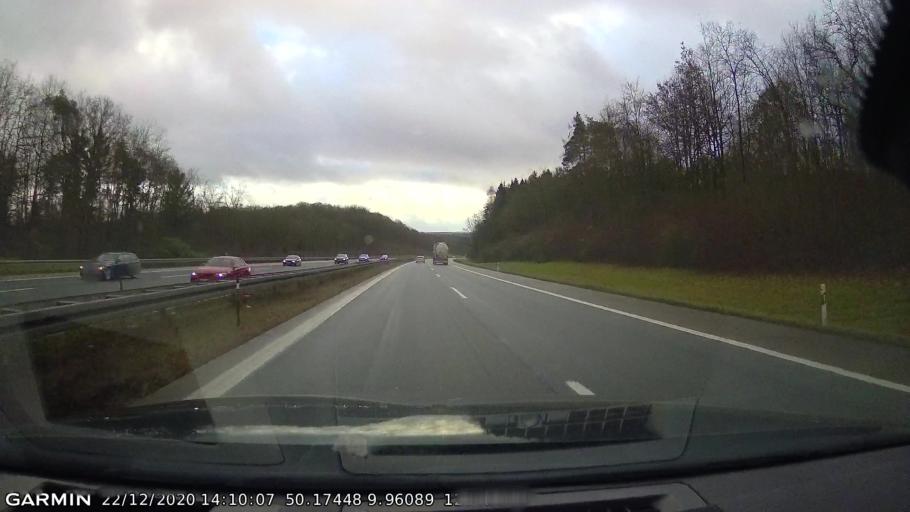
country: DE
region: Bavaria
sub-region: Regierungsbezirk Unterfranken
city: Oberthulba
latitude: 50.1741
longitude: 9.9610
